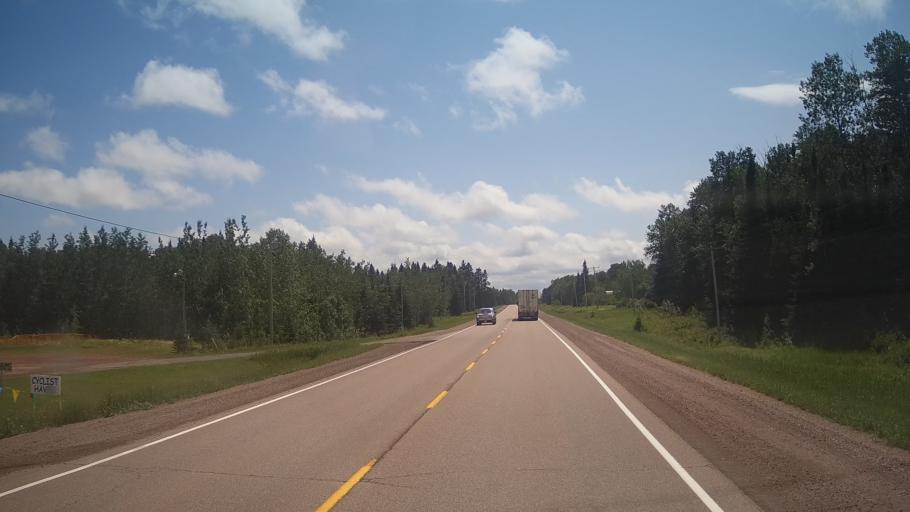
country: CA
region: Ontario
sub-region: Thunder Bay District
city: Thunder Bay
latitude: 48.8331
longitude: -88.5257
